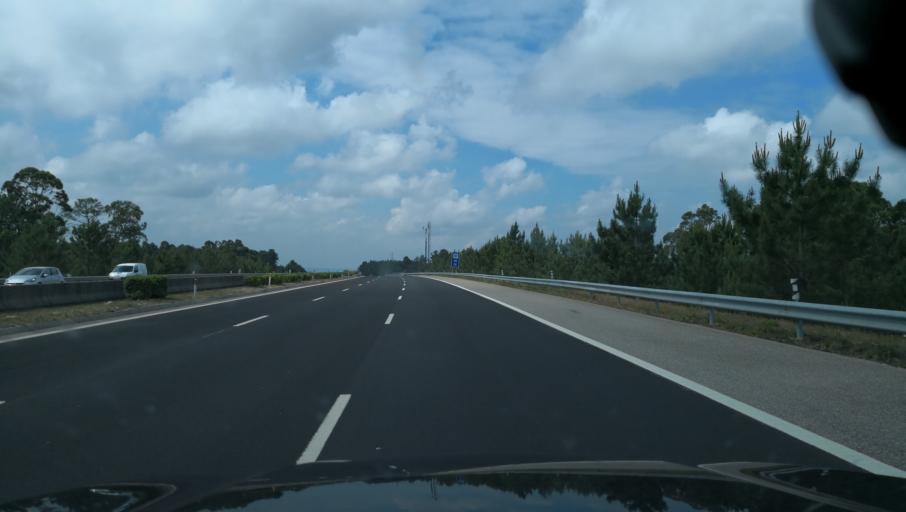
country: PT
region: Leiria
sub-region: Leiria
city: Maceira
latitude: 39.6909
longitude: -8.9317
